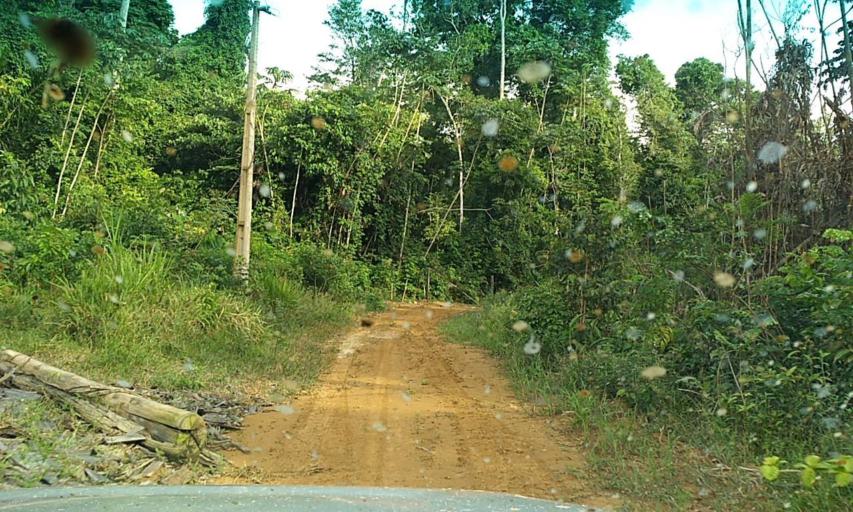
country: BR
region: Para
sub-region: Senador Jose Porfirio
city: Senador Jose Porfirio
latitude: -2.9920
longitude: -51.7443
